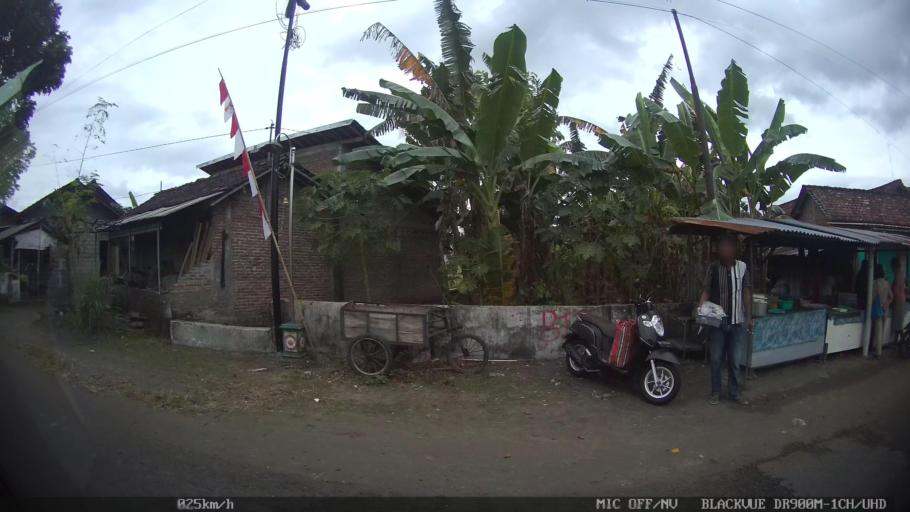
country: ID
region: Daerah Istimewa Yogyakarta
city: Sewon
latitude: -7.8653
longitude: 110.4028
